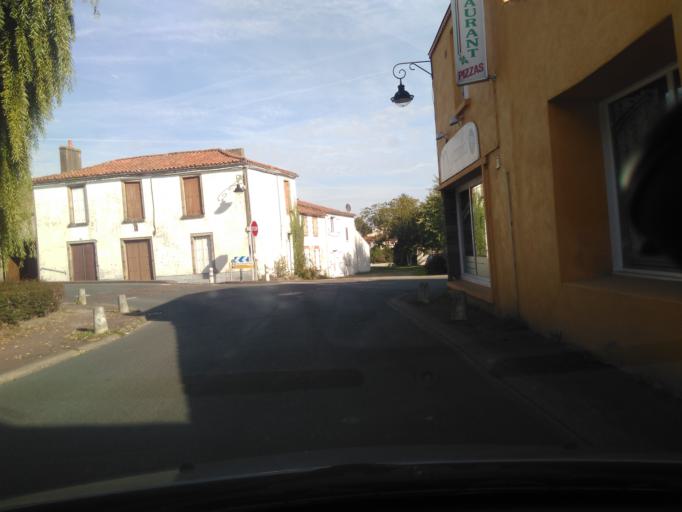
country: FR
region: Pays de la Loire
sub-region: Departement de la Vendee
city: Aubigny
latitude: 46.5954
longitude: -1.4536
